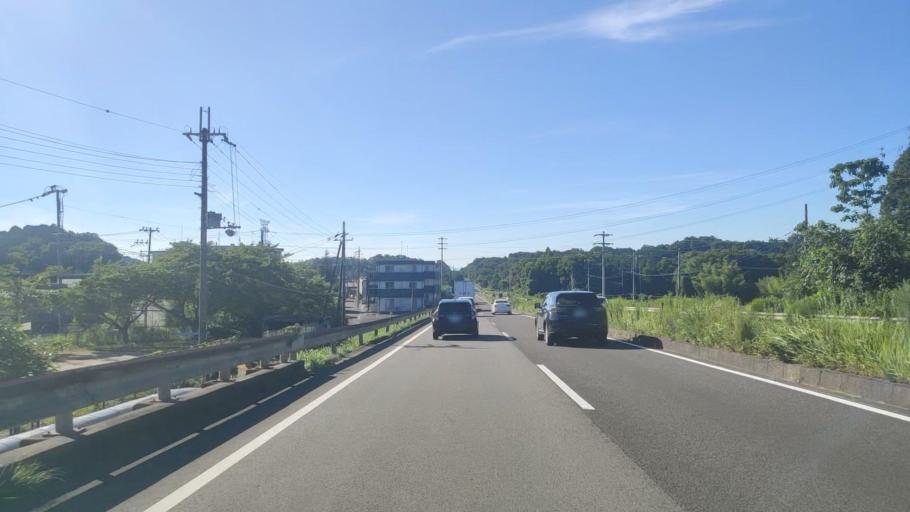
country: JP
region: Shiga Prefecture
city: Minakuchicho-matoba
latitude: 34.9641
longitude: 136.1982
